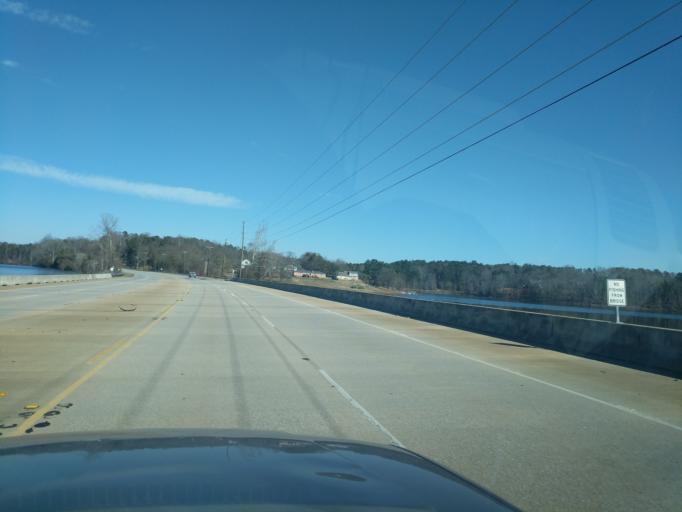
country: US
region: South Carolina
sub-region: Spartanburg County
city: Mayo
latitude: 35.0657
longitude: -81.8778
